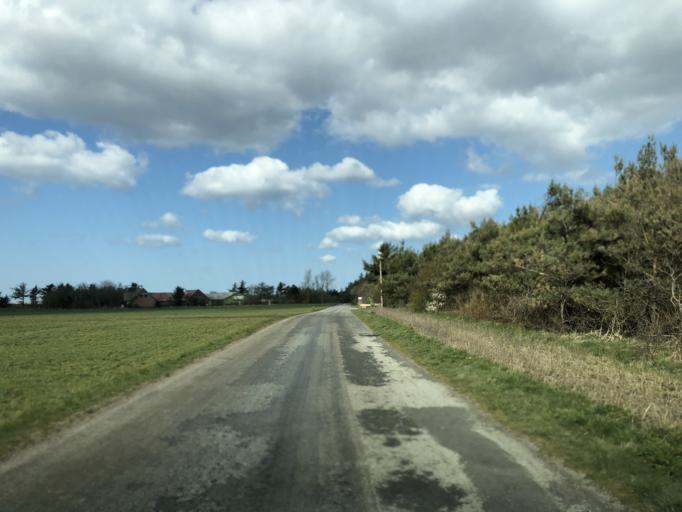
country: DK
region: Central Jutland
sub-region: Holstebro Kommune
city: Ulfborg
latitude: 56.3757
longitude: 8.2105
